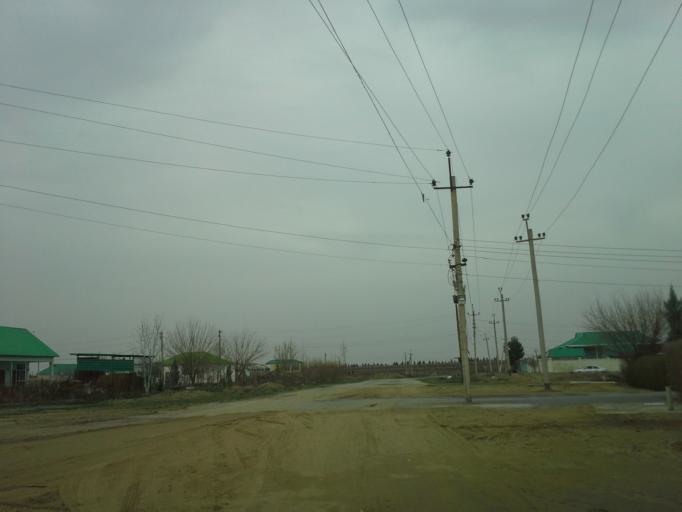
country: TM
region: Ahal
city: Abadan
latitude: 37.9764
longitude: 58.2260
